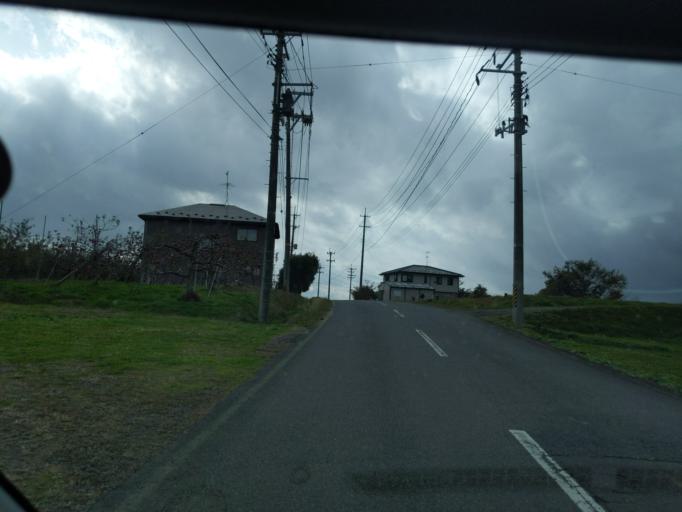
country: JP
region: Iwate
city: Mizusawa
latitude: 39.0601
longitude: 141.1184
